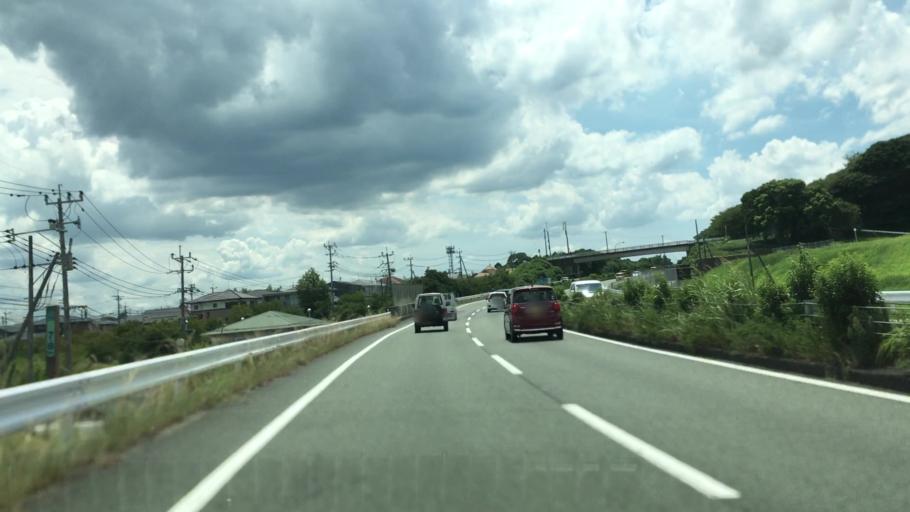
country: JP
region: Saga Prefecture
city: Tosu
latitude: 33.4038
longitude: 130.5135
